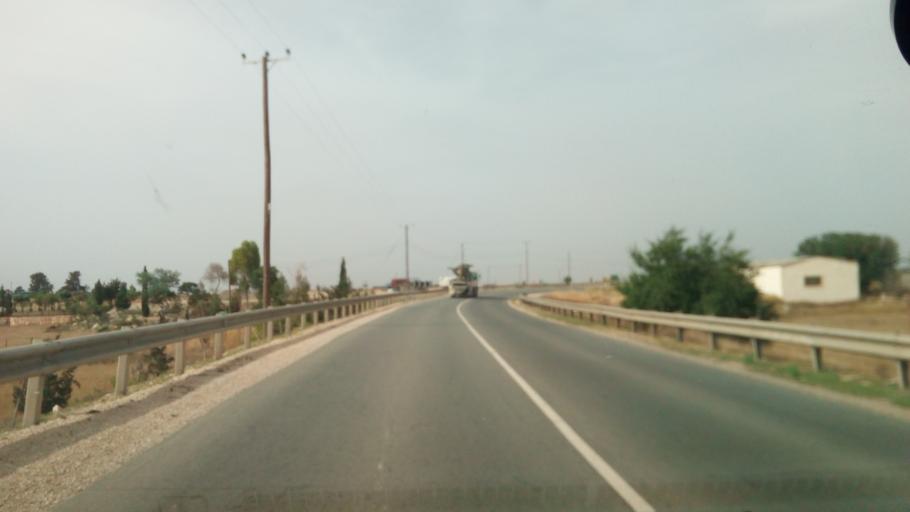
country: CY
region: Larnaka
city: Xylotymbou
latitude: 35.0210
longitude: 33.7371
